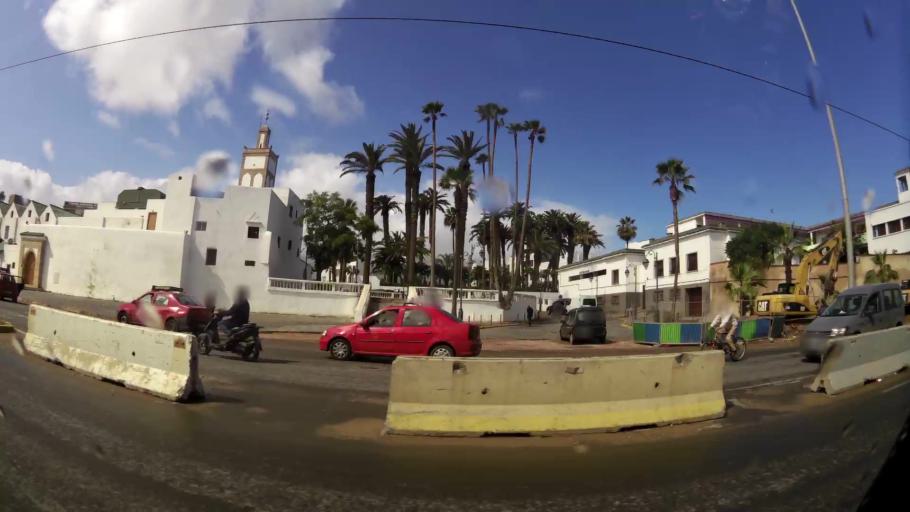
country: MA
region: Grand Casablanca
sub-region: Casablanca
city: Casablanca
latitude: 33.6021
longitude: -7.6180
